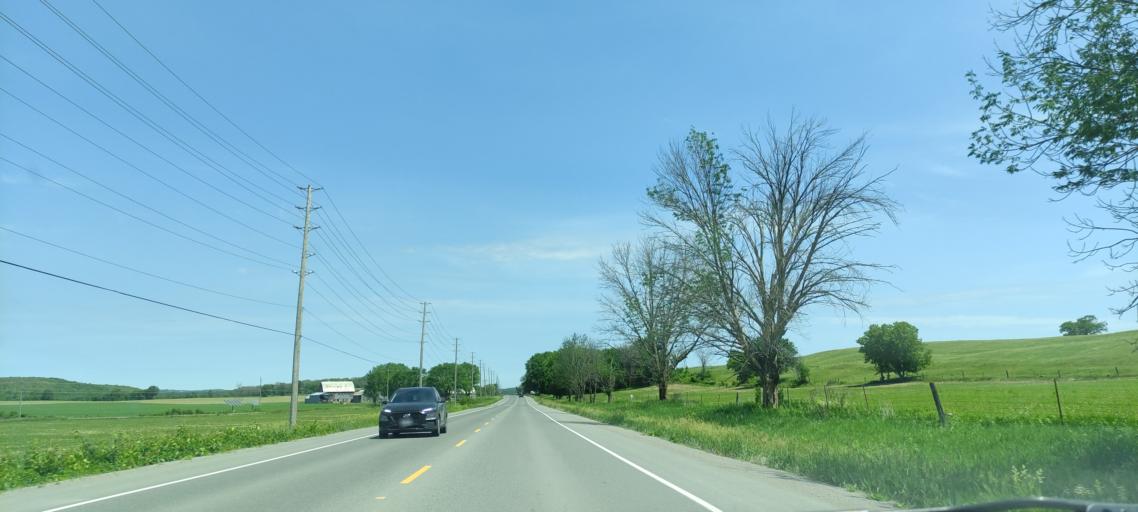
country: CA
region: Ontario
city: Quinte West
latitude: 44.2241
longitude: -77.8251
